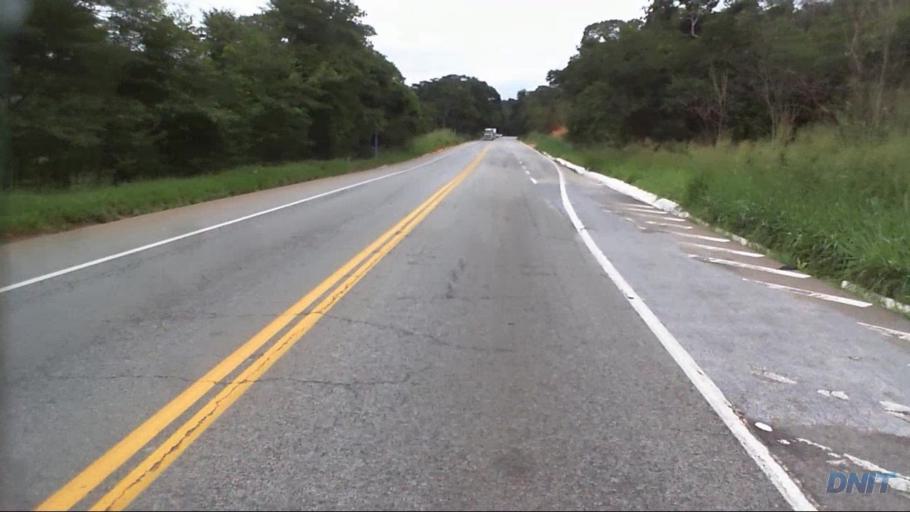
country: BR
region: Minas Gerais
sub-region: Barao De Cocais
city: Barao de Cocais
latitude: -19.8019
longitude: -43.4119
